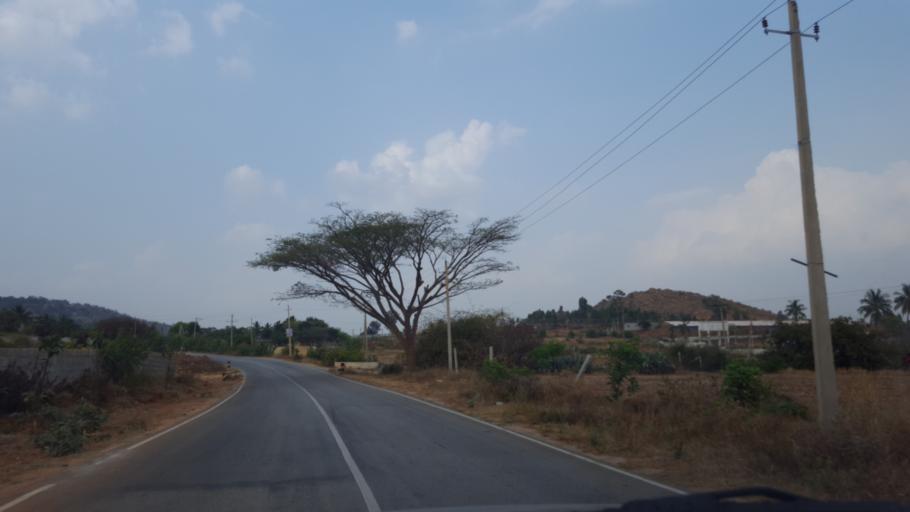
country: IN
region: Karnataka
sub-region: Chikkaballapur
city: Chik Ballapur
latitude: 13.3568
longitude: 77.6920
